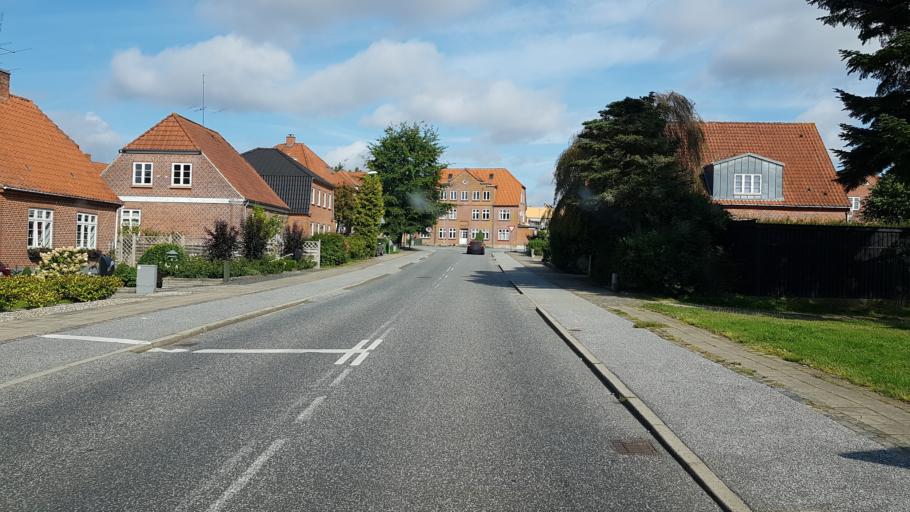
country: DK
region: South Denmark
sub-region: Haderslev Kommune
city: Haderslev
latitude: 55.2507
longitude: 9.4685
